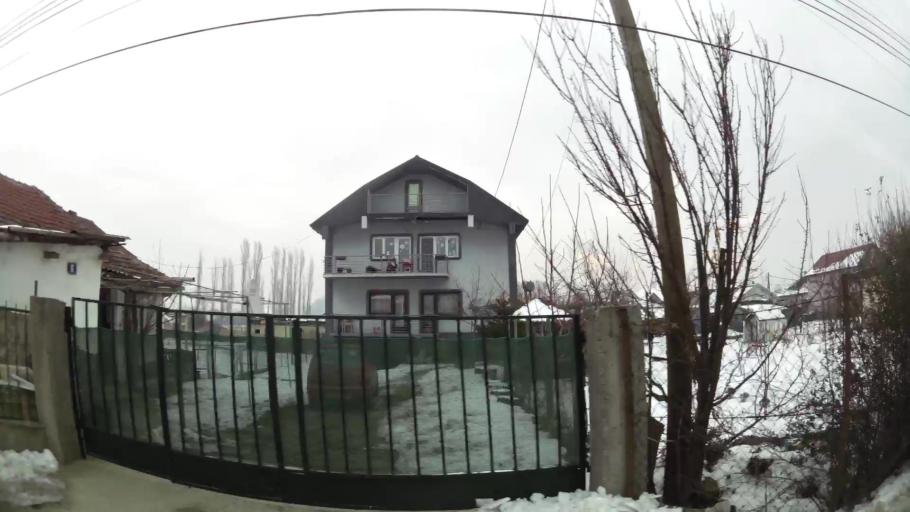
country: MK
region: Saraj
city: Saraj
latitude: 42.0462
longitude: 21.3582
